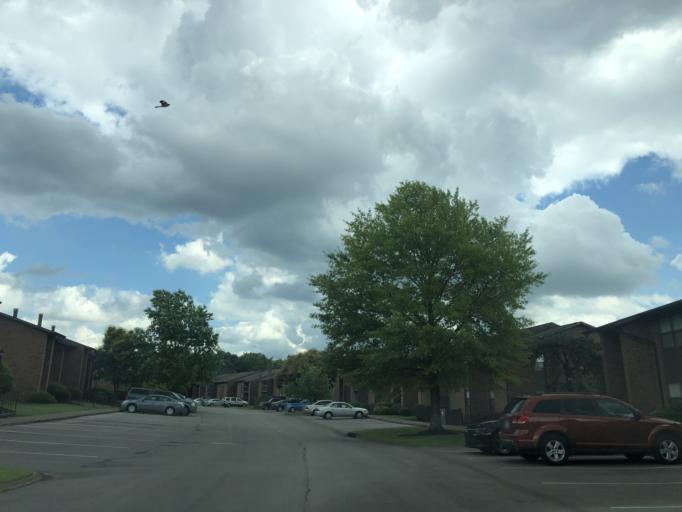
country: US
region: Tennessee
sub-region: Davidson County
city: Nashville
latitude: 36.2242
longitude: -86.7644
